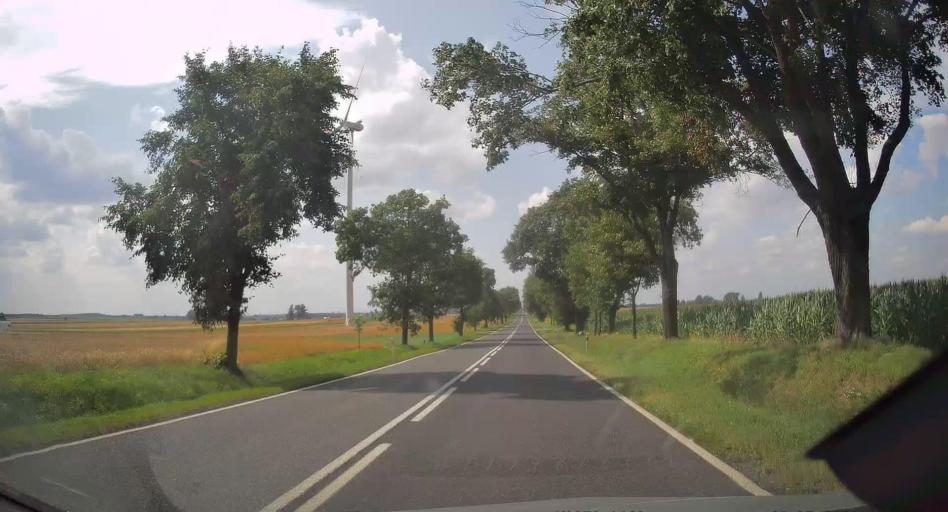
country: PL
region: Lodz Voivodeship
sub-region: Powiat skierniewicki
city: Gluchow
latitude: 51.7910
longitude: 20.0423
